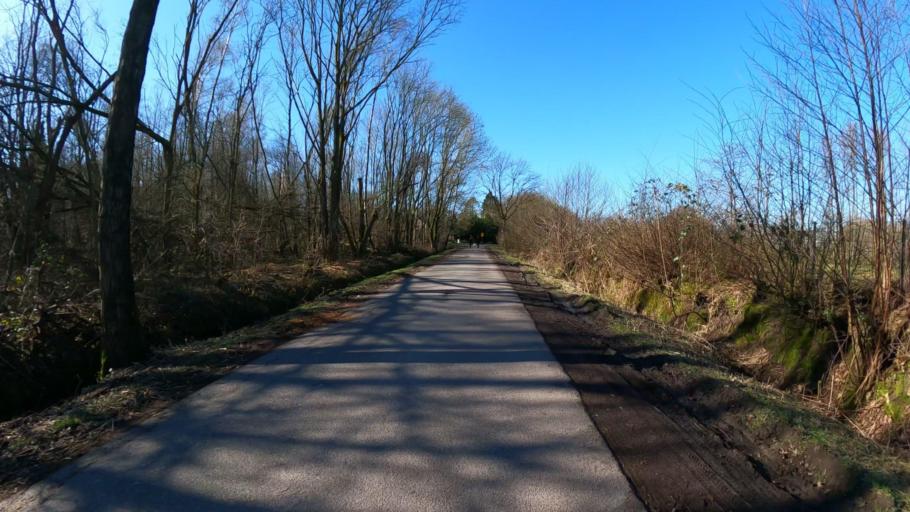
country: DE
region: Schleswig-Holstein
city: Kummerfeld
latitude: 53.6835
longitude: 9.7811
